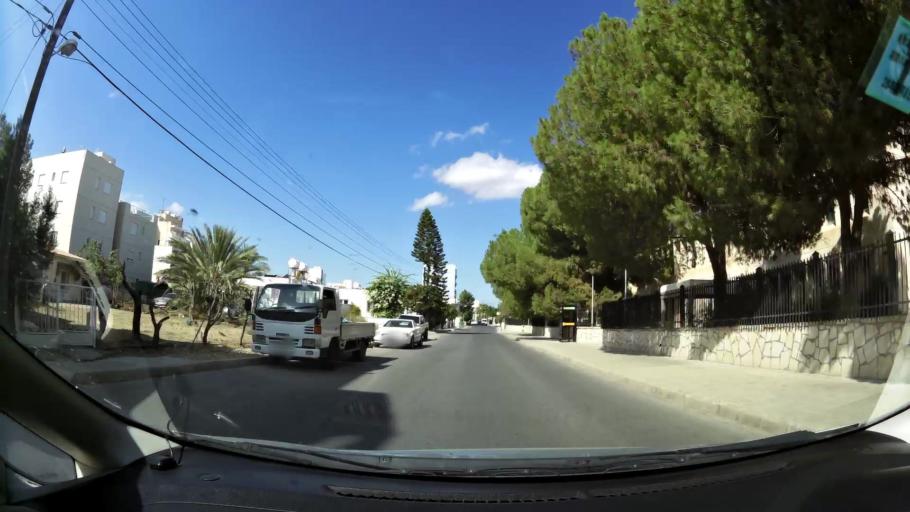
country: CY
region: Lefkosia
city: Nicosia
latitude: 35.1431
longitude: 33.3692
